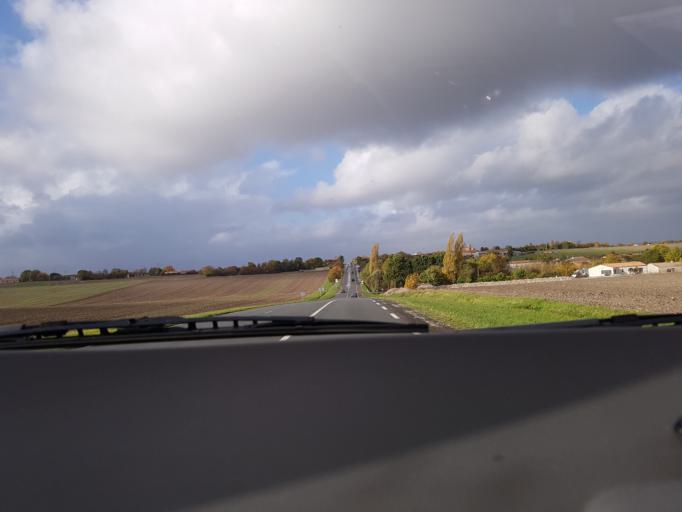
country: FR
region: Poitou-Charentes
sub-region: Departement de la Charente-Maritime
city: Thenac
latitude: 45.6476
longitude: -0.5841
